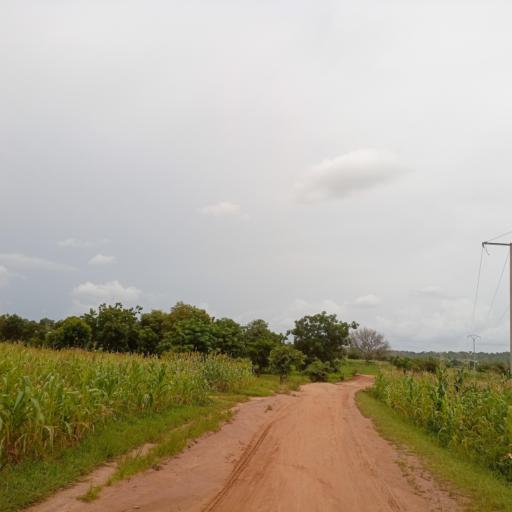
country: TG
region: Savanes
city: Dapaong
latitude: 10.8094
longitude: 0.0270
